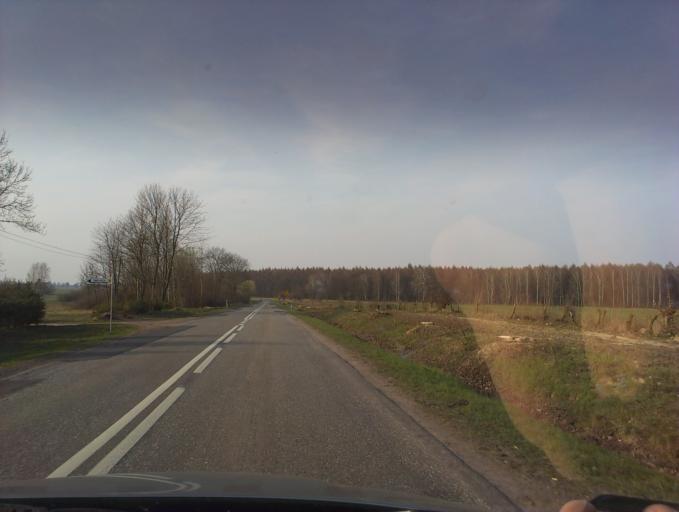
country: PL
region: Greater Poland Voivodeship
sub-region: Powiat zlotowski
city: Lipka
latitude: 53.5091
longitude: 17.2425
